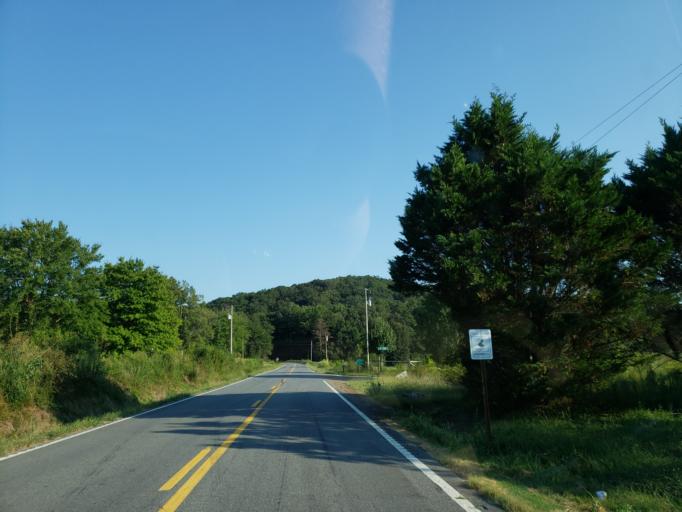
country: US
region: Tennessee
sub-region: Bradley County
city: Wildwood Lake
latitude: 35.0062
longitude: -84.7855
